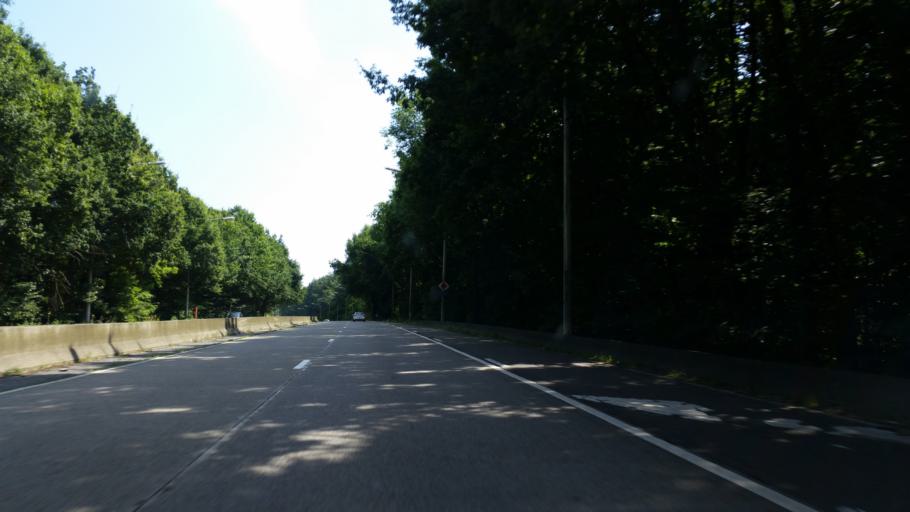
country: BE
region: Wallonia
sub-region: Province de Namur
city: Hamois
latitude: 50.2834
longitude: 5.1861
